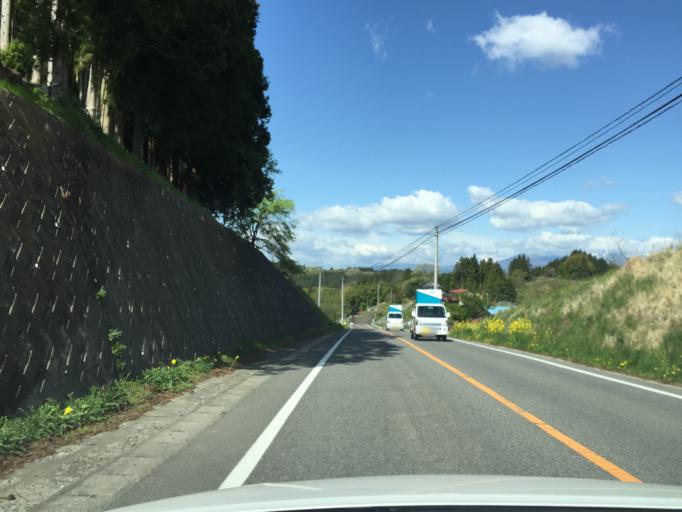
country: JP
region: Fukushima
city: Funehikimachi-funehiki
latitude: 37.5402
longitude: 140.5742
